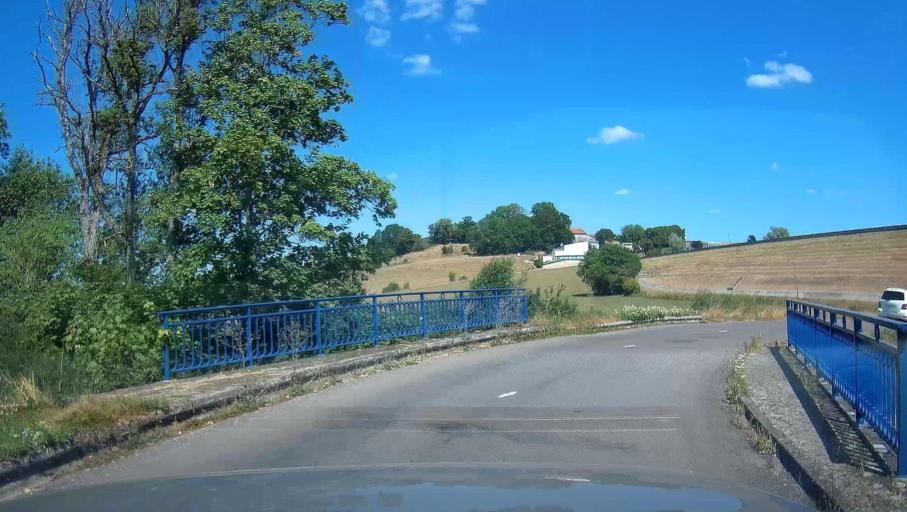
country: FR
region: Champagne-Ardenne
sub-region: Departement de la Haute-Marne
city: Langres
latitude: 47.8658
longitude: 5.3725
